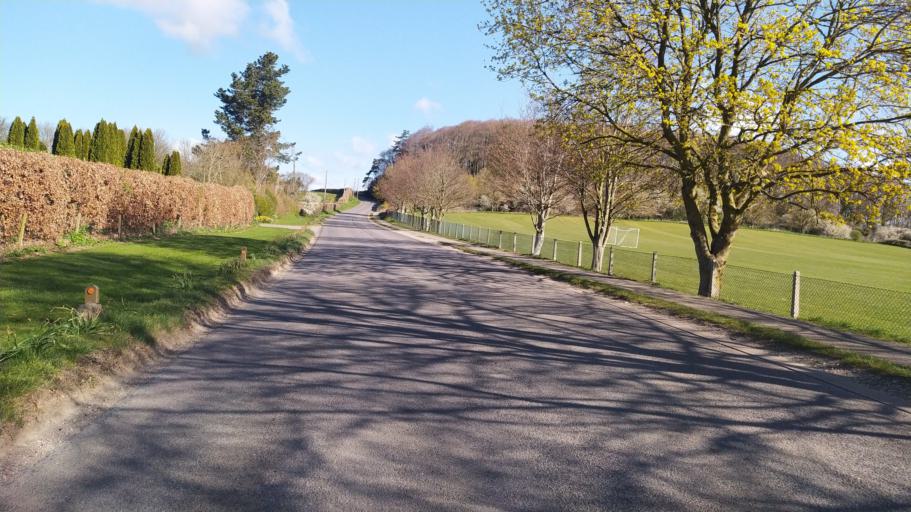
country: GB
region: England
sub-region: Dorset
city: Sturminster Newton
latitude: 50.9360
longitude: -2.3046
